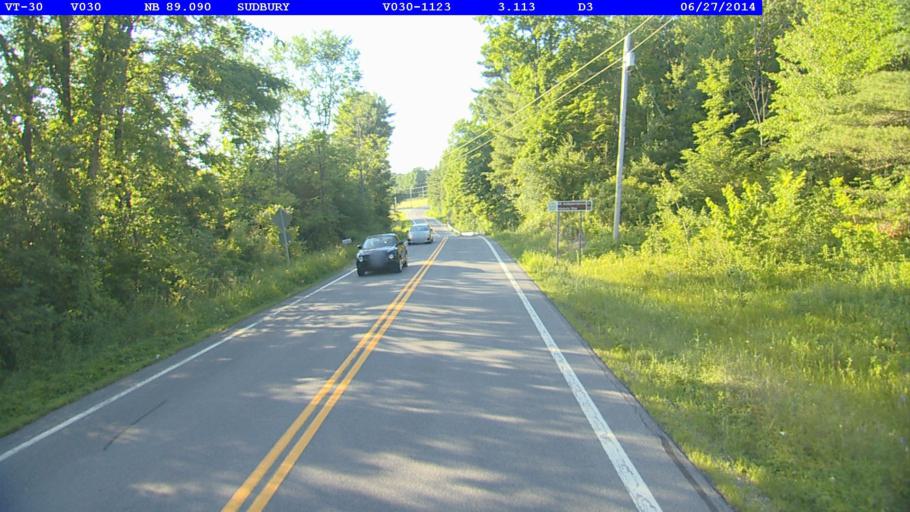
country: US
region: Vermont
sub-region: Rutland County
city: Brandon
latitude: 43.7929
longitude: -73.2047
